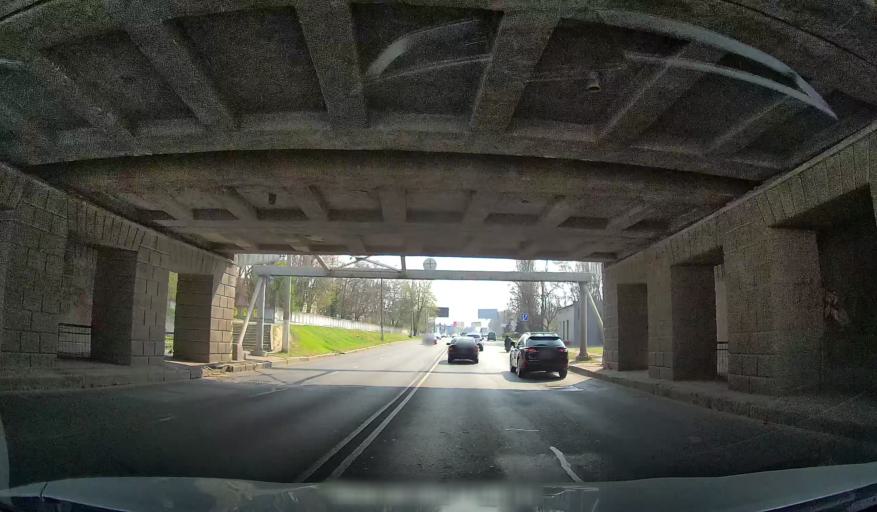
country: NG
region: Niger
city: Lemu
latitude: 9.2911
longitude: 6.1458
